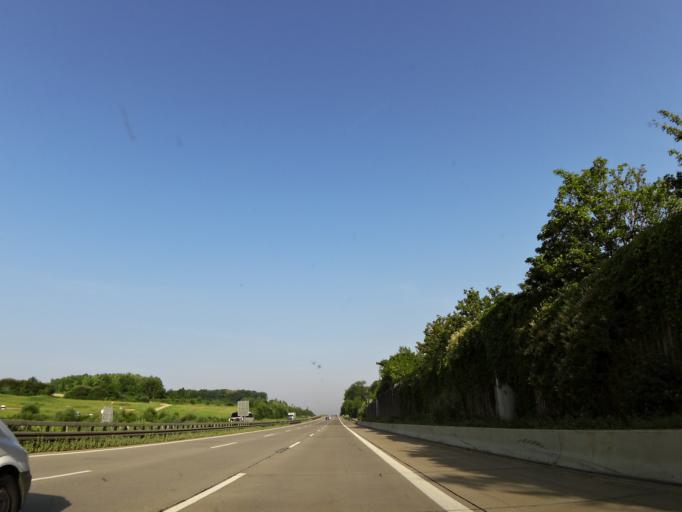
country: DE
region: Baden-Wuerttemberg
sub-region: Regierungsbezirk Stuttgart
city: Holzmaden
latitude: 48.6287
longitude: 9.5079
